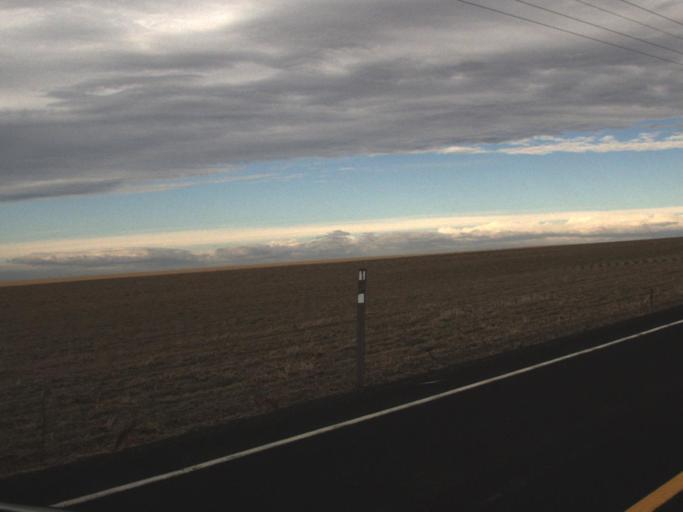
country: US
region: Washington
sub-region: Adams County
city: Ritzville
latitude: 47.4467
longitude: -118.7374
